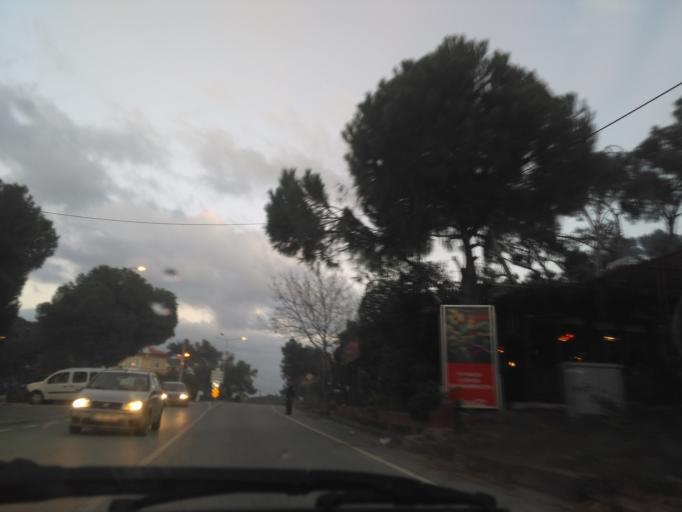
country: TR
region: Balikesir
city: Ayvalik
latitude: 39.2999
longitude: 26.6643
